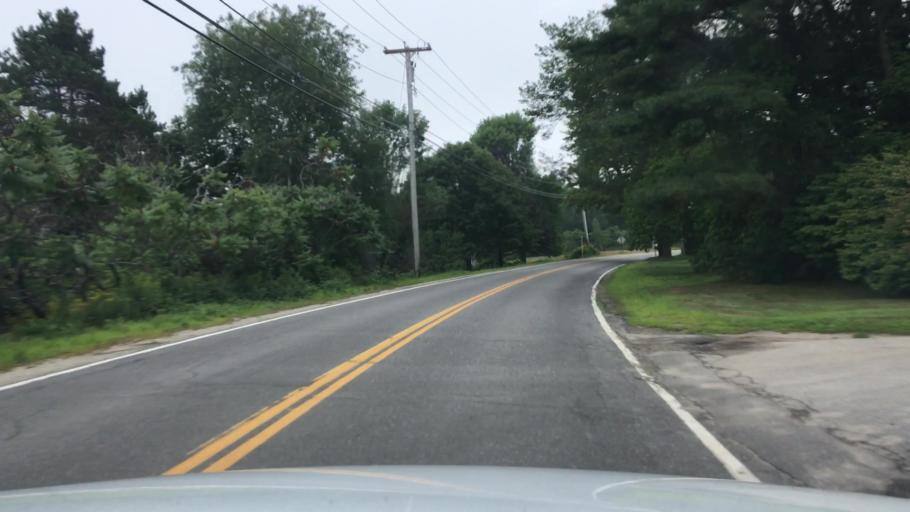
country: US
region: Maine
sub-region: Cumberland County
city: Harpswell Center
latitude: 43.7673
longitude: -69.9718
